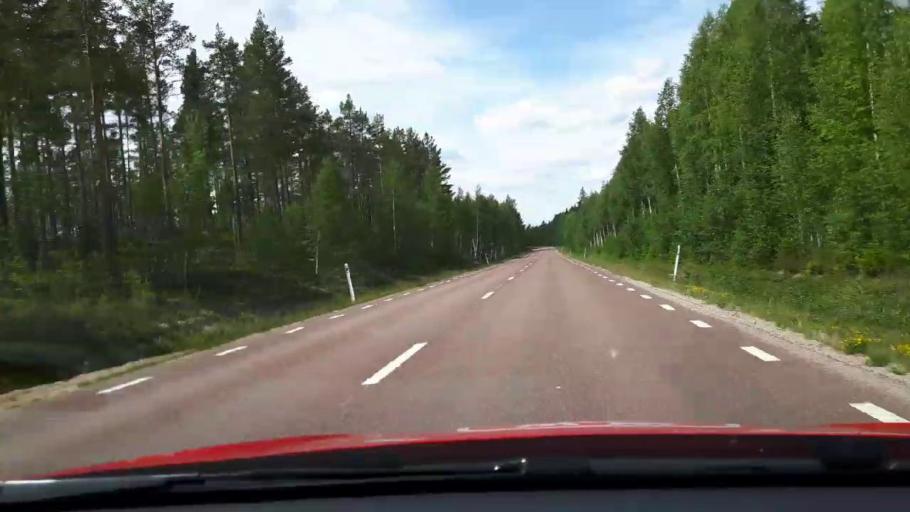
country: SE
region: Jaemtland
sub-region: Harjedalens Kommun
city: Sveg
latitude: 62.0455
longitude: 14.8507
